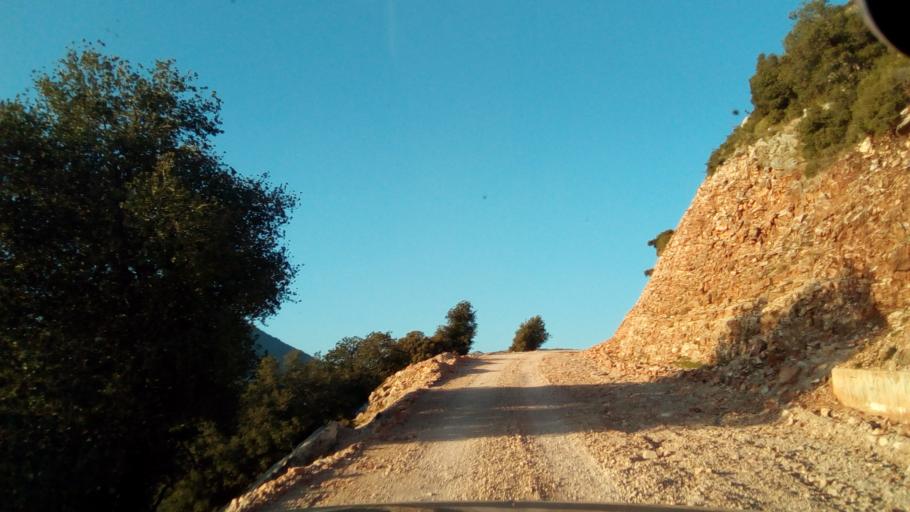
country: GR
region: West Greece
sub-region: Nomos Aitolias kai Akarnanias
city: Nafpaktos
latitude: 38.4442
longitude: 21.8428
